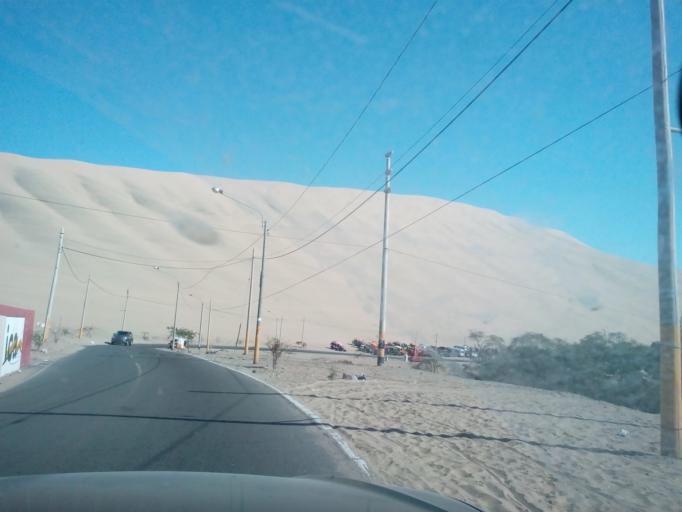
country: PE
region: Ica
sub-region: Provincia de Ica
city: Ica
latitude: -14.0869
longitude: -75.7605
